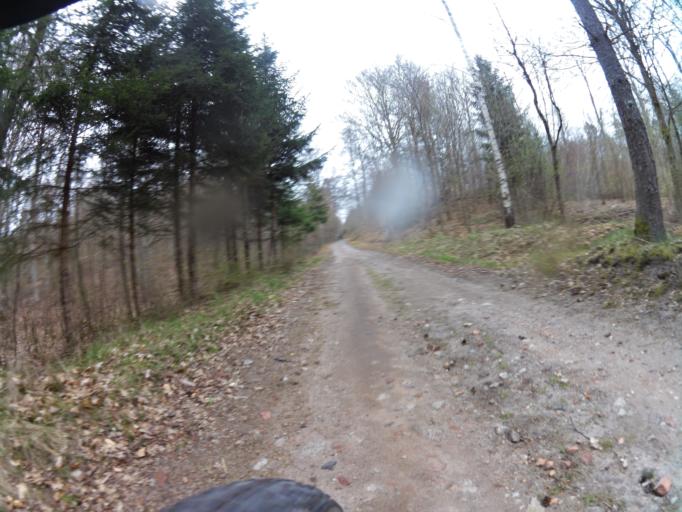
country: PL
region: West Pomeranian Voivodeship
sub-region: Powiat koszalinski
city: Polanow
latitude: 54.0495
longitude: 16.6216
